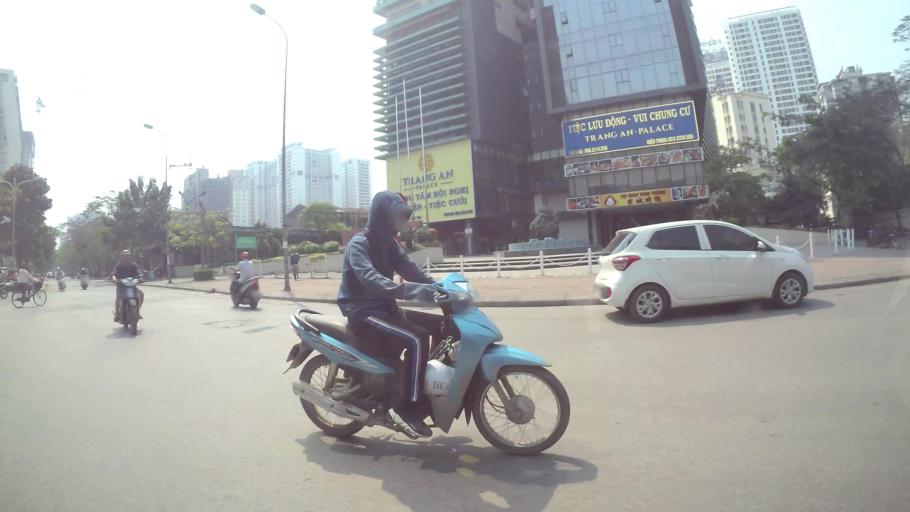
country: VN
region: Ha Noi
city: Thanh Xuan
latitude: 21.0025
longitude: 105.8058
